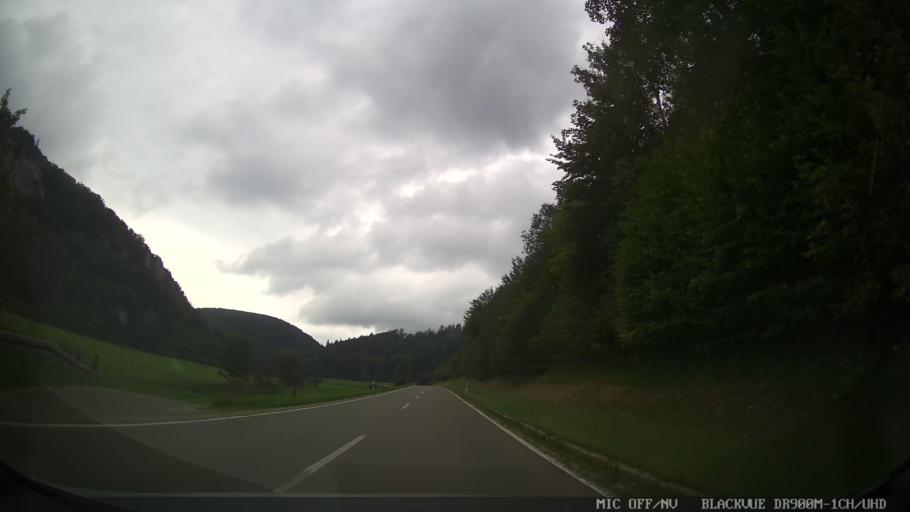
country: DE
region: Baden-Wuerttemberg
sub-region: Freiburg Region
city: Barenthal
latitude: 48.0654
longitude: 8.9255
